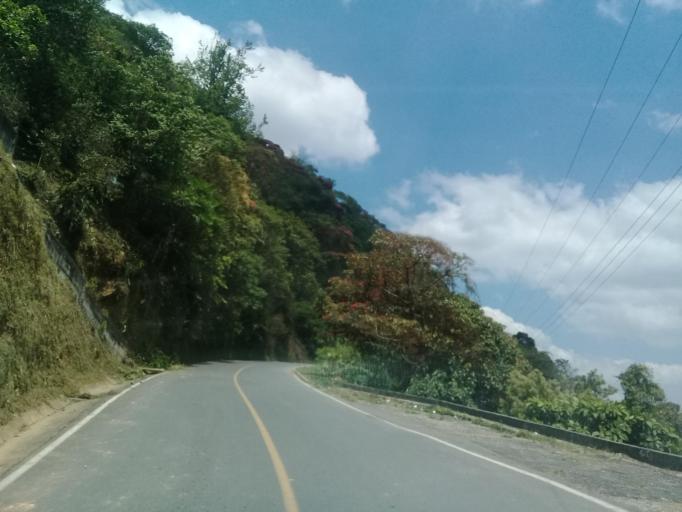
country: MX
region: Veracruz
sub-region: Tlilapan
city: Tonalixco
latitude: 18.7870
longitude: -97.0596
